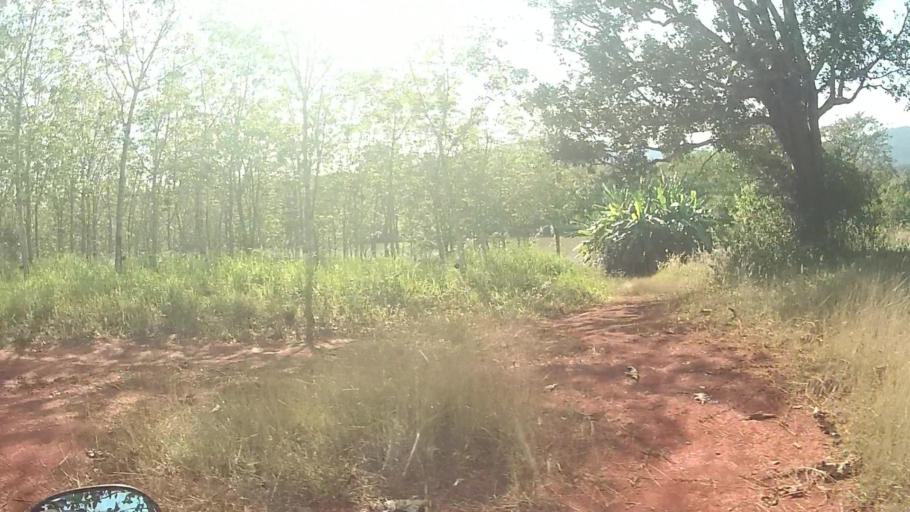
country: TH
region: Chiang Mai
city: Mae On
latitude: 18.9179
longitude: 99.2014
